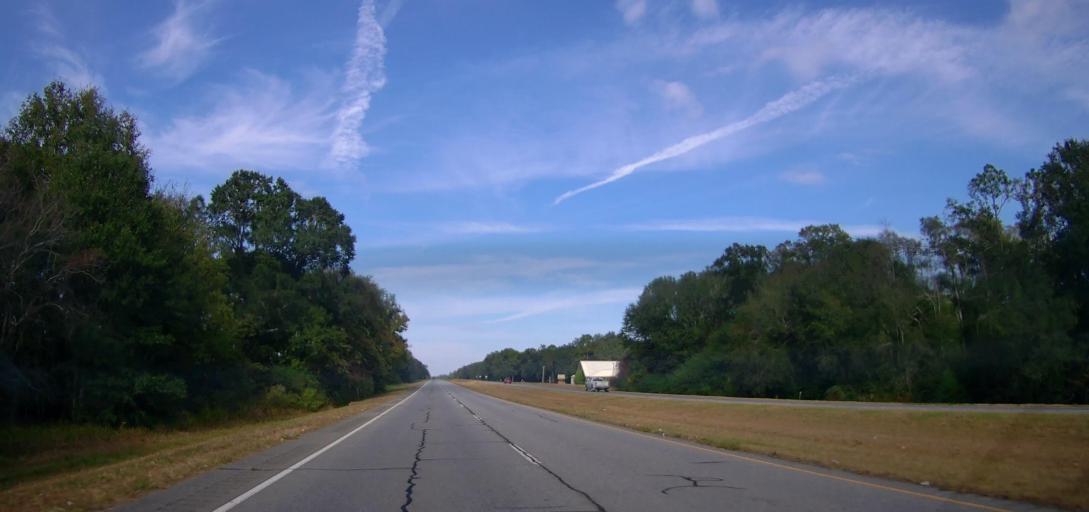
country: US
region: Georgia
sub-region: Mitchell County
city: Camilla
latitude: 31.2991
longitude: -84.1818
